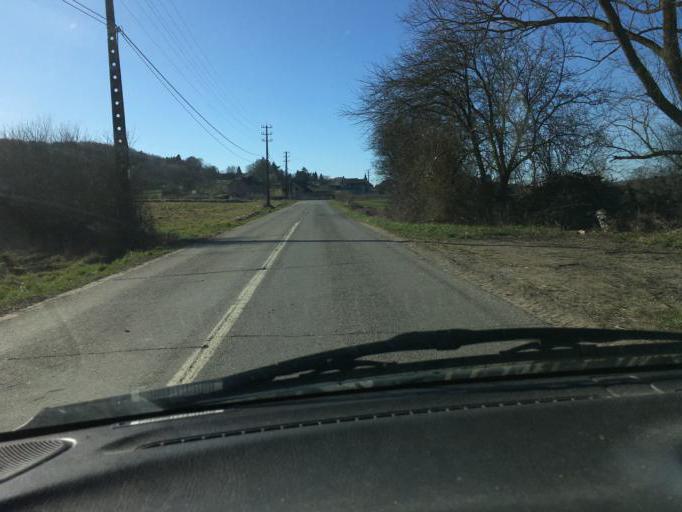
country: FR
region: Champagne-Ardenne
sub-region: Departement des Ardennes
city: Vireux-Molhain
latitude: 50.1173
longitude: 4.6331
